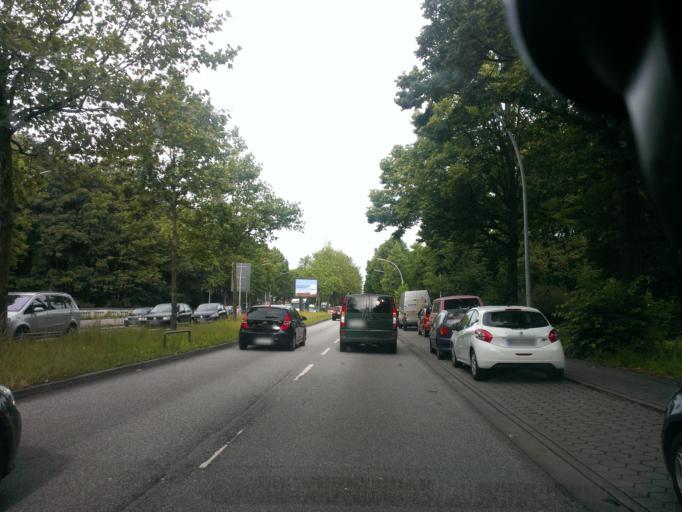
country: DE
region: Hamburg
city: Marienthal
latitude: 53.5596
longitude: 10.0678
